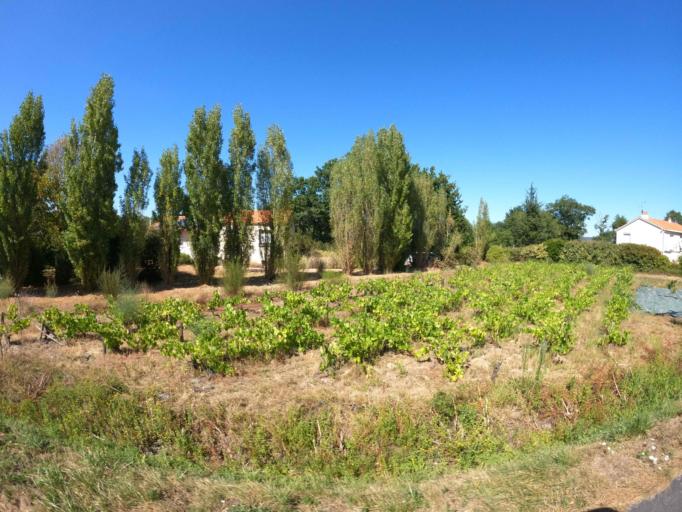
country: FR
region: Pays de la Loire
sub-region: Departement de la Vendee
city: La Guyonniere
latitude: 46.9557
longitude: -1.2270
